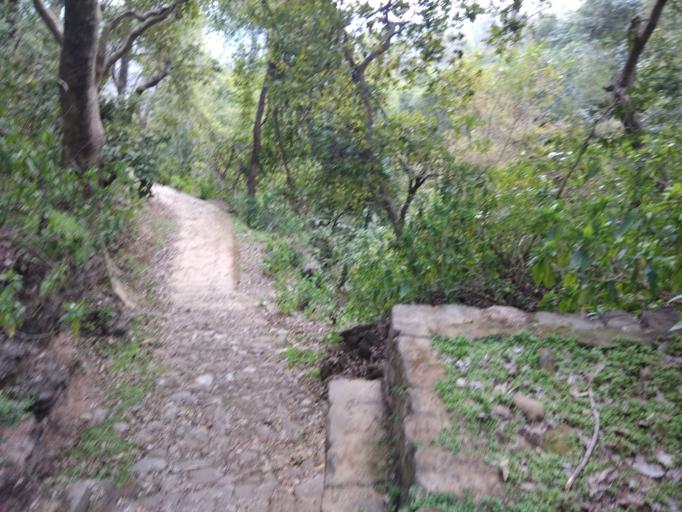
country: IN
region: Himachal Pradesh
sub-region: Kangra
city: Kotla
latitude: 32.2355
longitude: 76.0440
